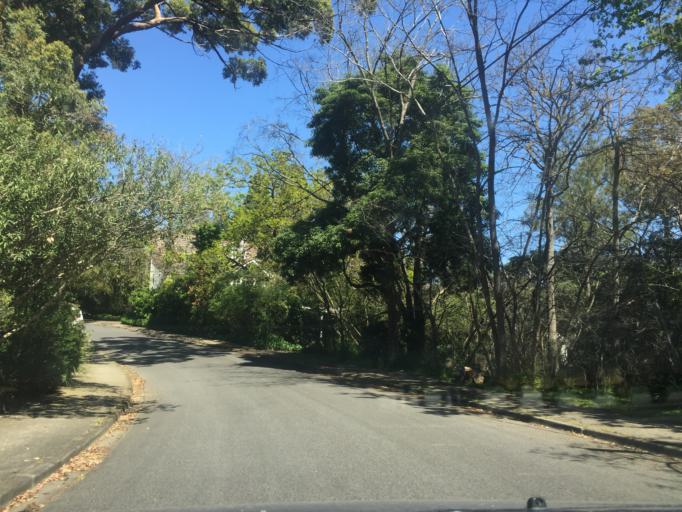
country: AU
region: Victoria
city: Ivanhoe East
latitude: -37.7680
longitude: 145.0612
